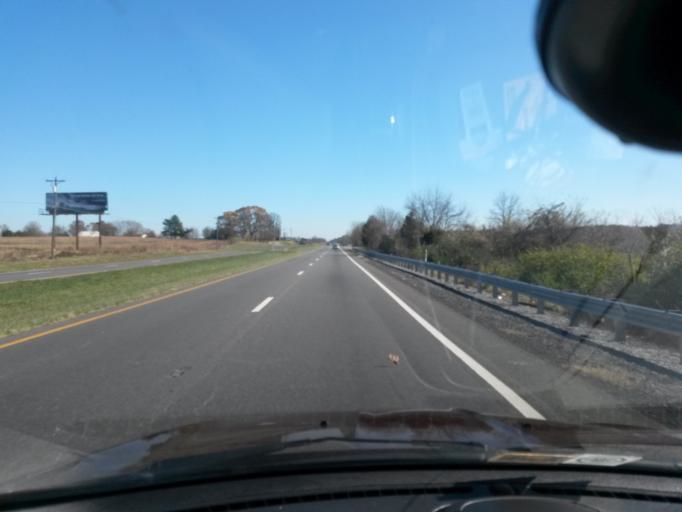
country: US
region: Virginia
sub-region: Bedford County
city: Forest
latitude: 37.3004
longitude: -79.3684
